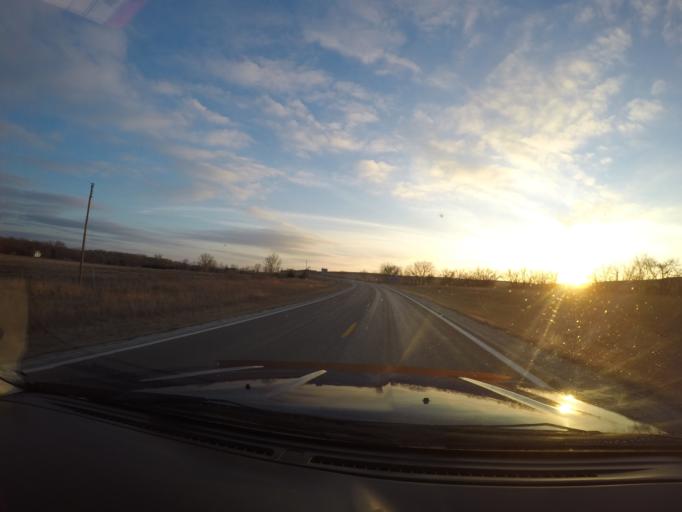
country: US
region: Kansas
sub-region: Chase County
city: Cottonwood Falls
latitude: 38.4453
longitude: -96.5562
